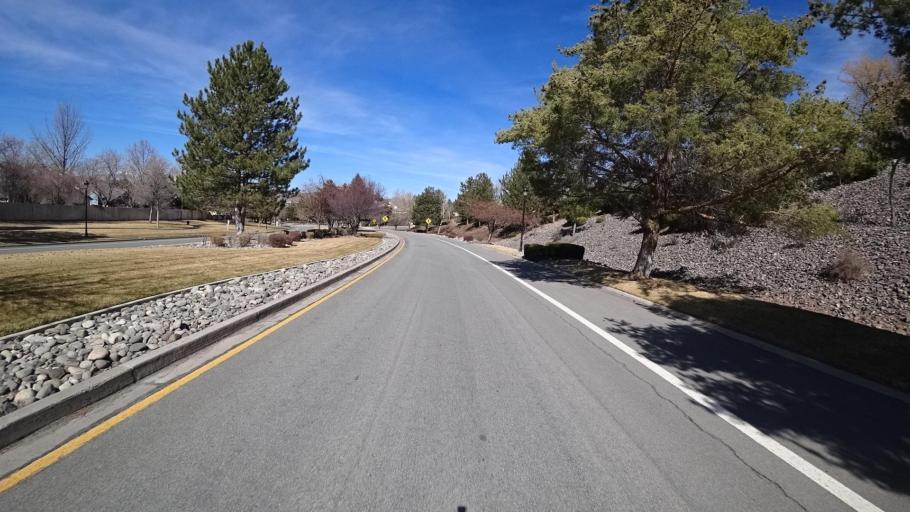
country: US
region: Nevada
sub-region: Washoe County
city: Spanish Springs
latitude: 39.5838
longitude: -119.7042
